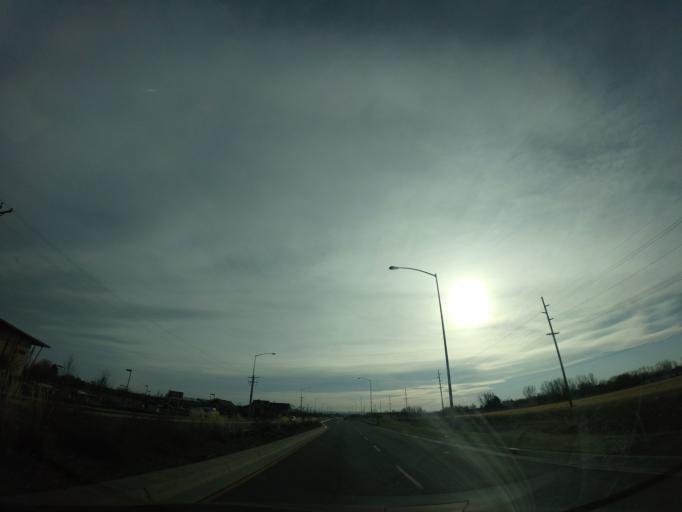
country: US
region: Montana
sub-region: Yellowstone County
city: Billings
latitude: 45.7741
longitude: -108.6176
